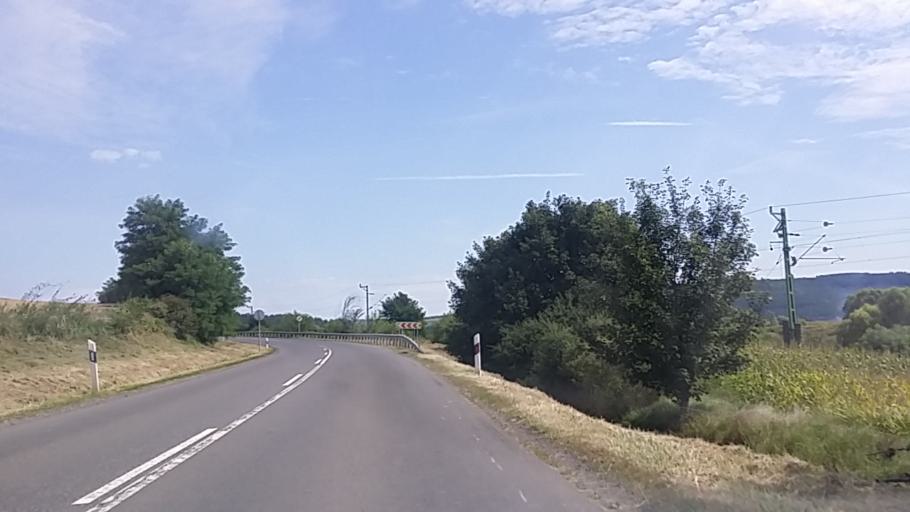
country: HU
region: Baranya
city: Sasd
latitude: 46.2853
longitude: 18.1170
